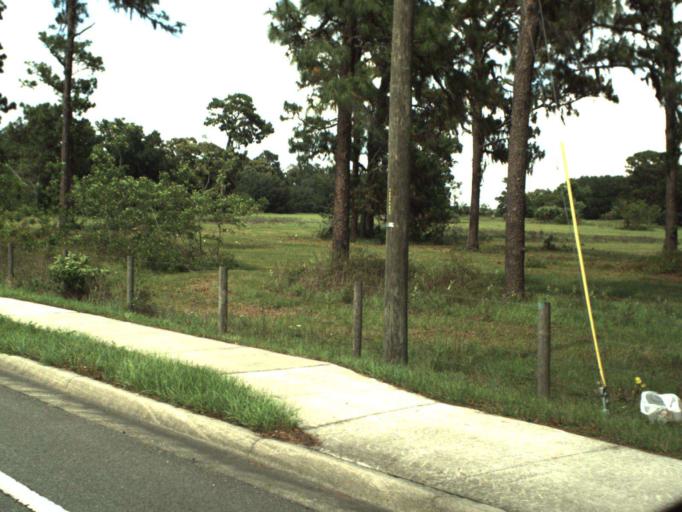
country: US
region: Florida
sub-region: Marion County
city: Silver Springs Shores
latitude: 29.1737
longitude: -82.0535
